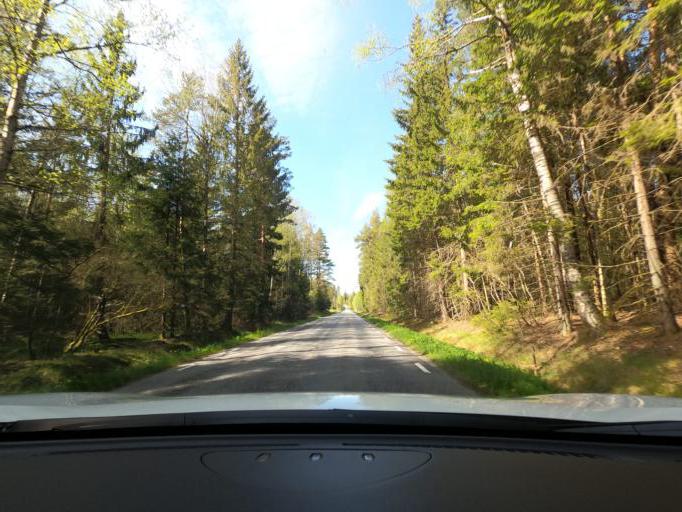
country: SE
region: Vaestra Goetaland
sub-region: Marks Kommun
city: Bua
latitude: 57.4833
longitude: 12.5665
